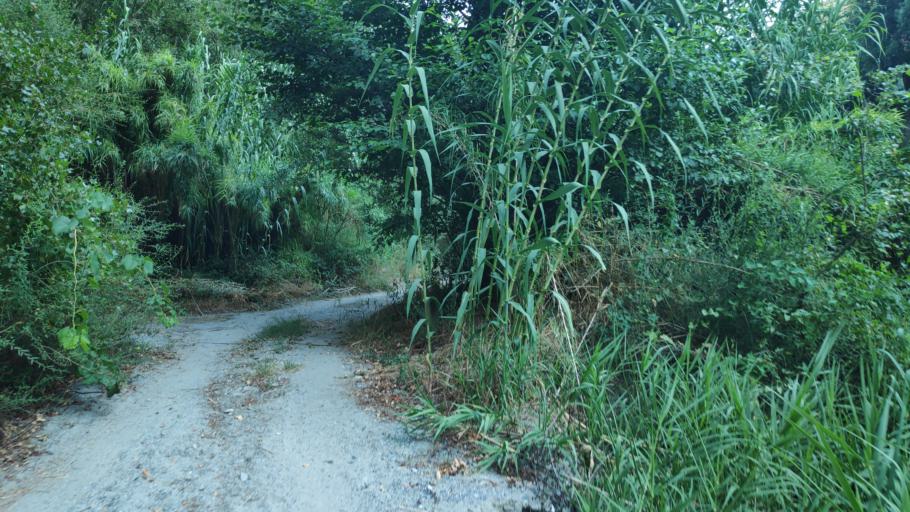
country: IT
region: Calabria
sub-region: Provincia di Reggio Calabria
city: Placanica
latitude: 38.4158
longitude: 16.4369
